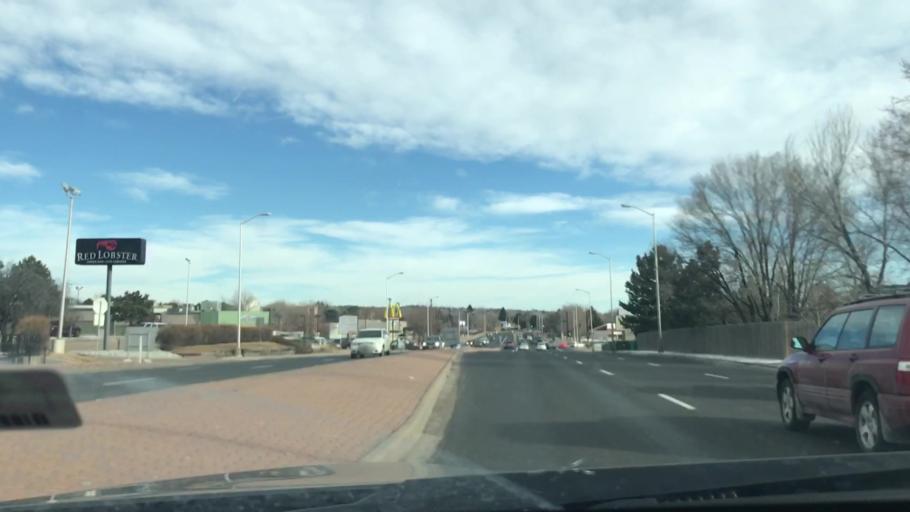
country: US
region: Colorado
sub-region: El Paso County
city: Cimarron Hills
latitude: 38.9024
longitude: -104.7704
